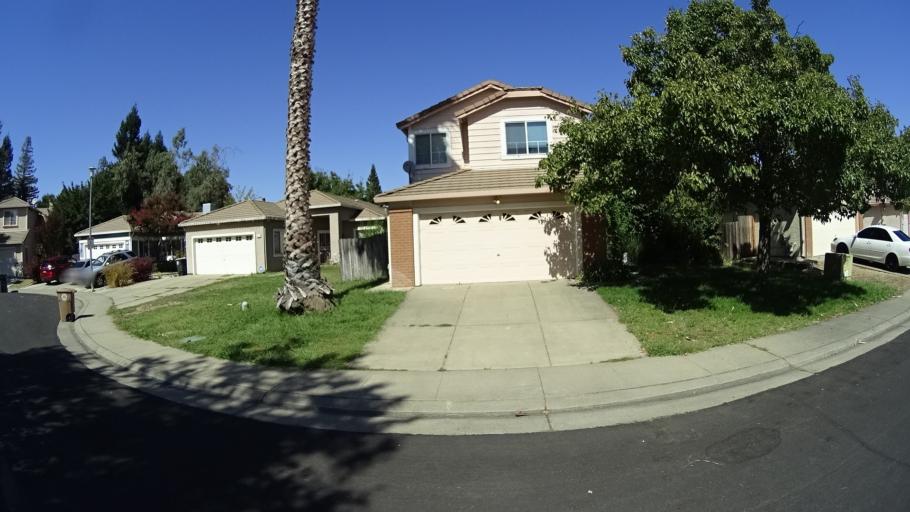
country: US
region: California
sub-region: Sacramento County
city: Laguna
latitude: 38.4310
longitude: -121.4405
